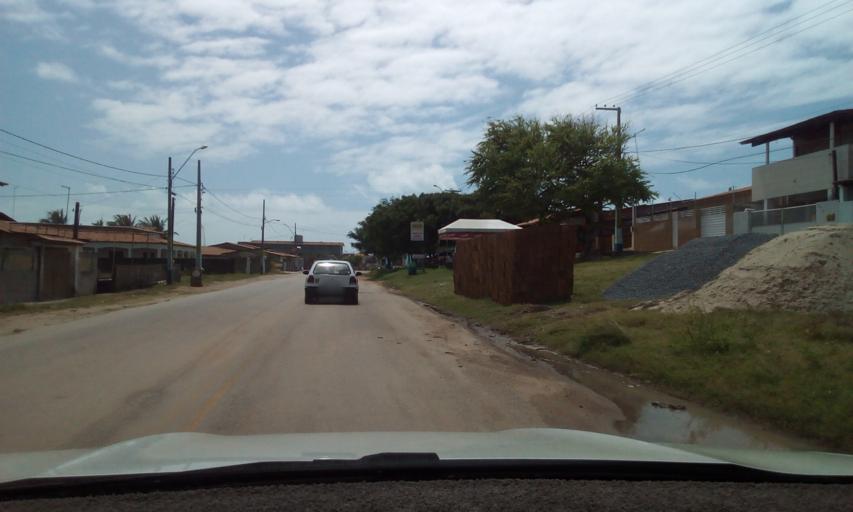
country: BR
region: Paraiba
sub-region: Rio Tinto
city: Rio Tinto
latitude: -6.6927
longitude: -34.9351
